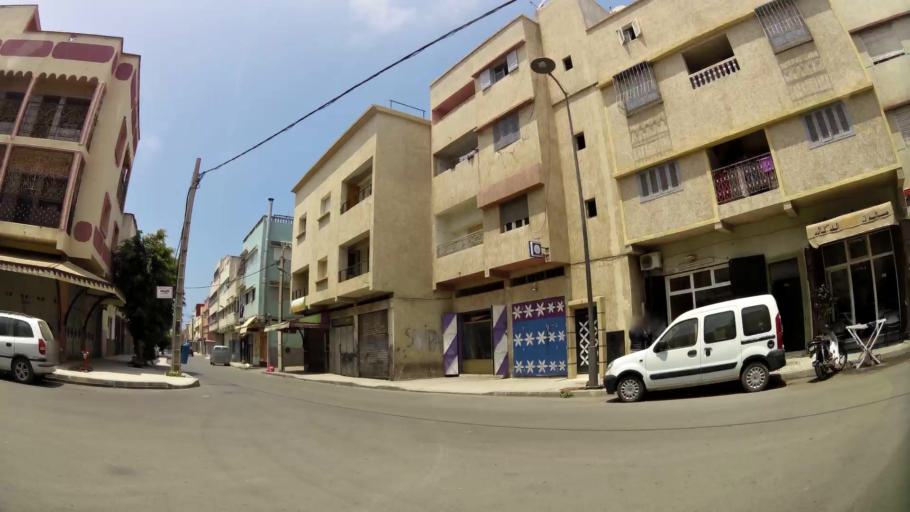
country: MA
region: Rabat-Sale-Zemmour-Zaer
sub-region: Skhirate-Temara
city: Temara
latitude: 33.9795
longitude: -6.8862
